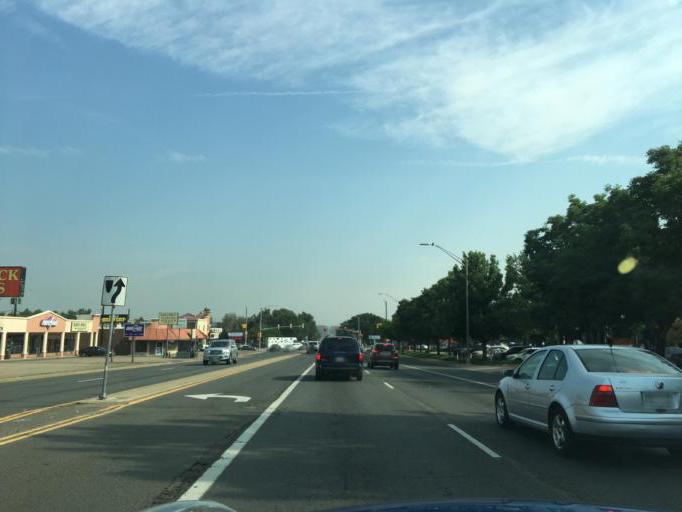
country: US
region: Colorado
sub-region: Jefferson County
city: Wheat Ridge
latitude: 39.7751
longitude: -105.0814
